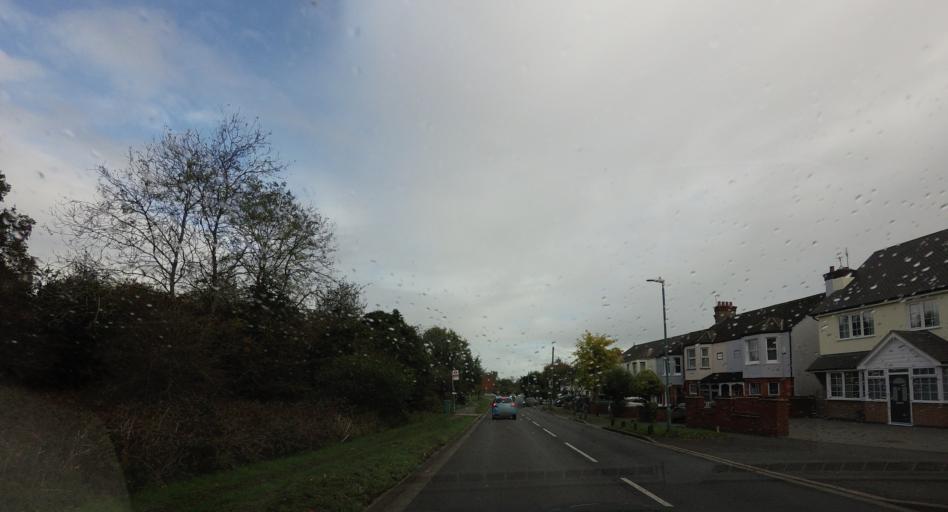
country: GB
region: England
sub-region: Kent
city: Dartford
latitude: 51.4322
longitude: 0.1861
